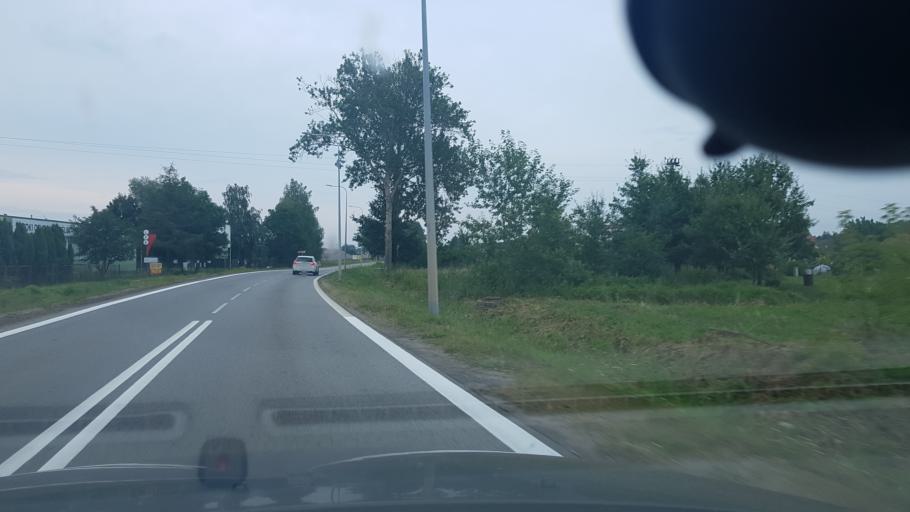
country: PL
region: Pomeranian Voivodeship
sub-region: Powiat nowodworski
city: Nowy Dwor Gdanski
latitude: 54.2155
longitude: 19.1070
